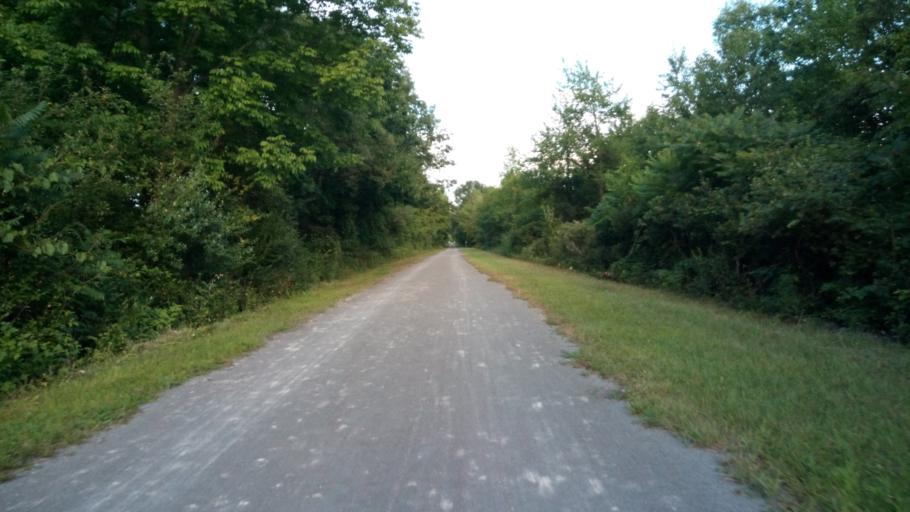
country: US
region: New York
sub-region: Ontario County
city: Victor
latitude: 43.0014
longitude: -77.4637
